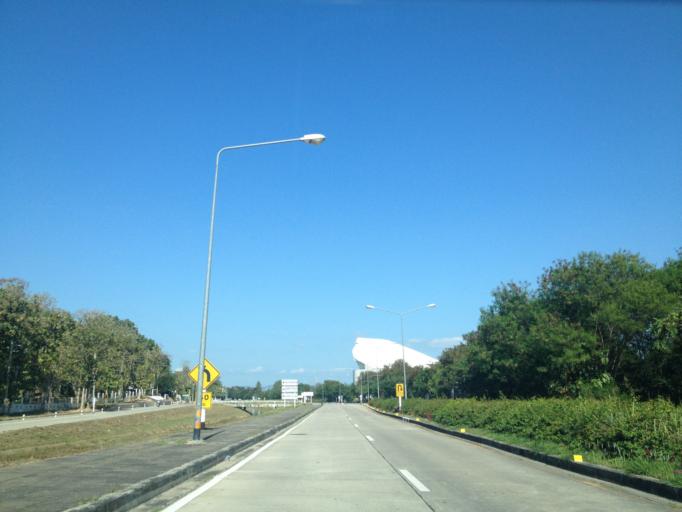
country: TH
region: Chiang Mai
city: Chiang Mai
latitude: 18.8475
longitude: 98.9598
